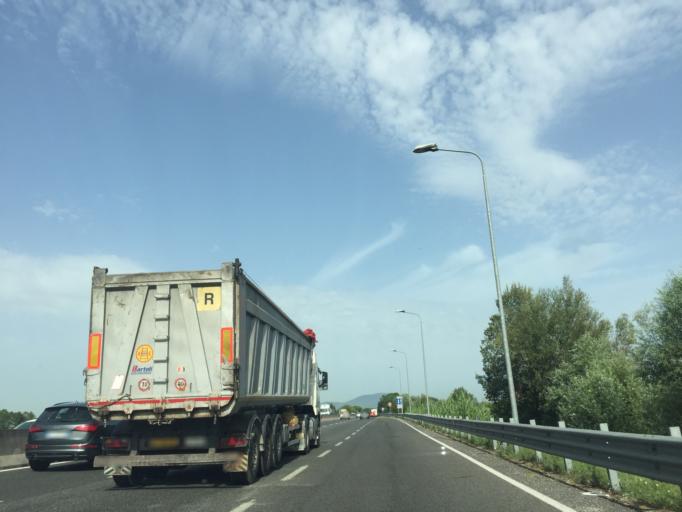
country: IT
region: Tuscany
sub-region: Province of Pisa
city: San Miniato Basso
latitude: 43.6973
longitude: 10.8254
